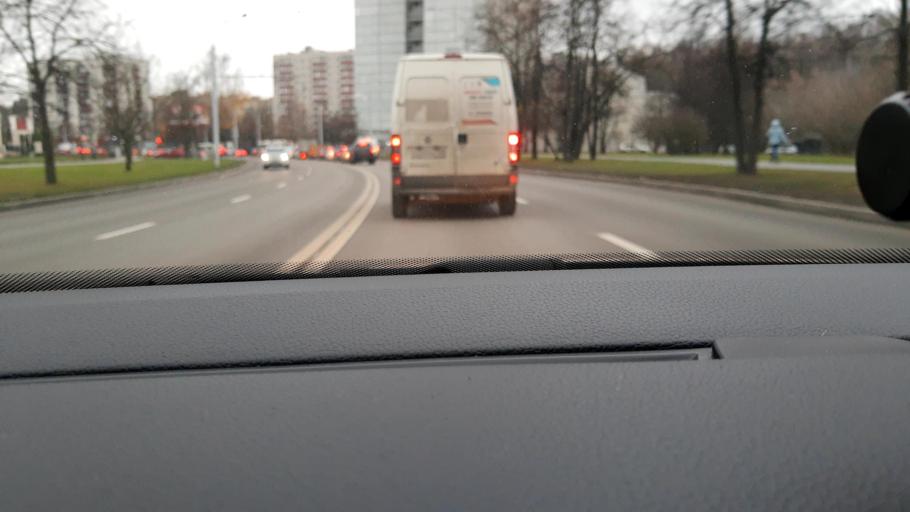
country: RU
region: Moscow
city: Gol'yanovo
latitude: 55.8233
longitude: 37.8008
